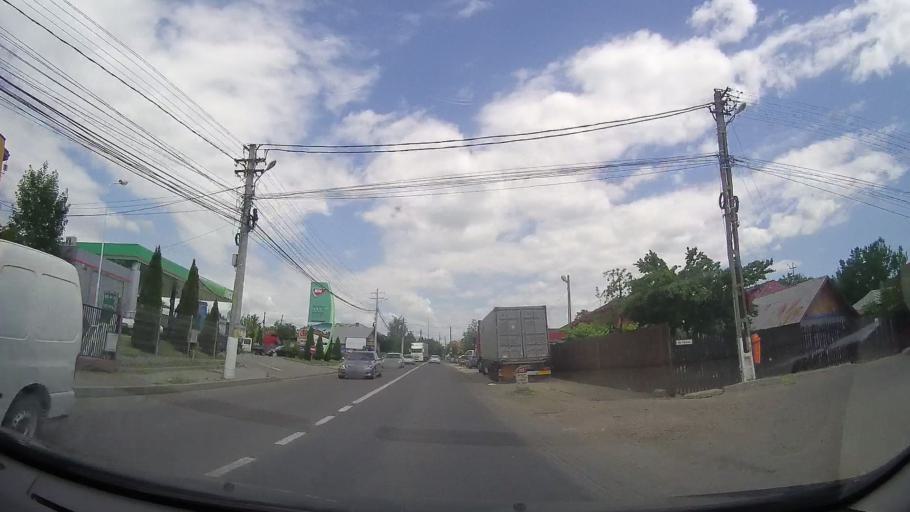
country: RO
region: Prahova
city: Valenii de Munte
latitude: 45.1923
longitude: 26.0430
